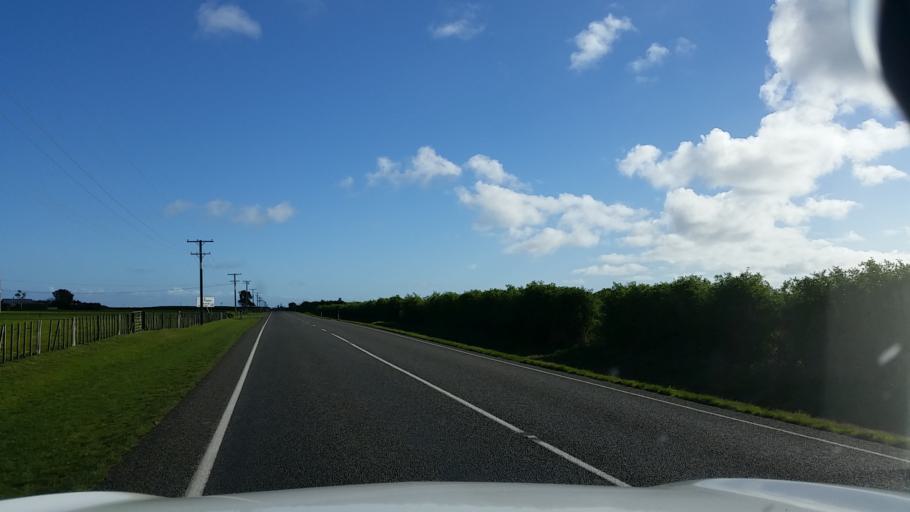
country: NZ
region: Taranaki
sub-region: South Taranaki District
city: Patea
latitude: -39.7466
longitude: 174.5161
